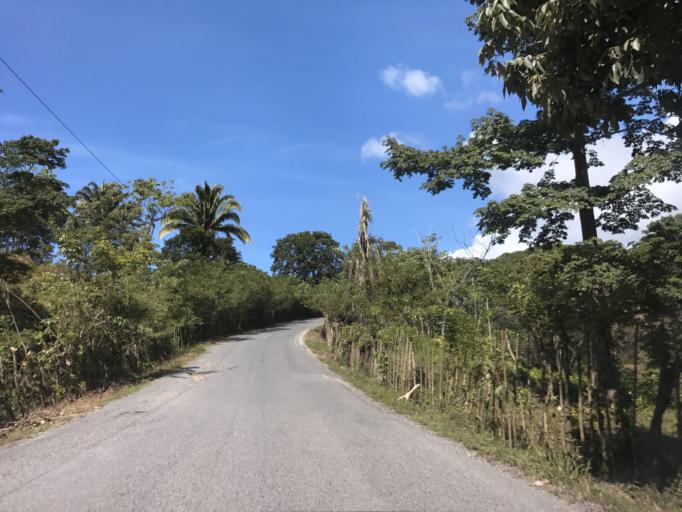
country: GT
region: Izabal
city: Morales
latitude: 15.6399
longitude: -89.0312
